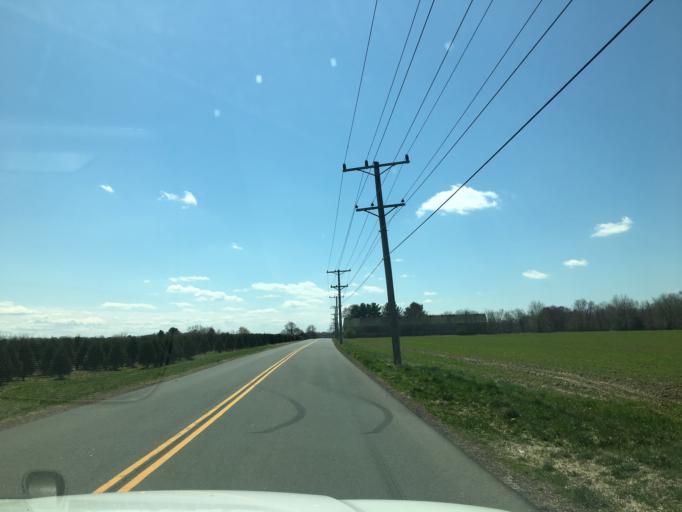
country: US
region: Connecticut
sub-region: Hartford County
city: Hazardville
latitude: 42.0008
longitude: -72.5303
